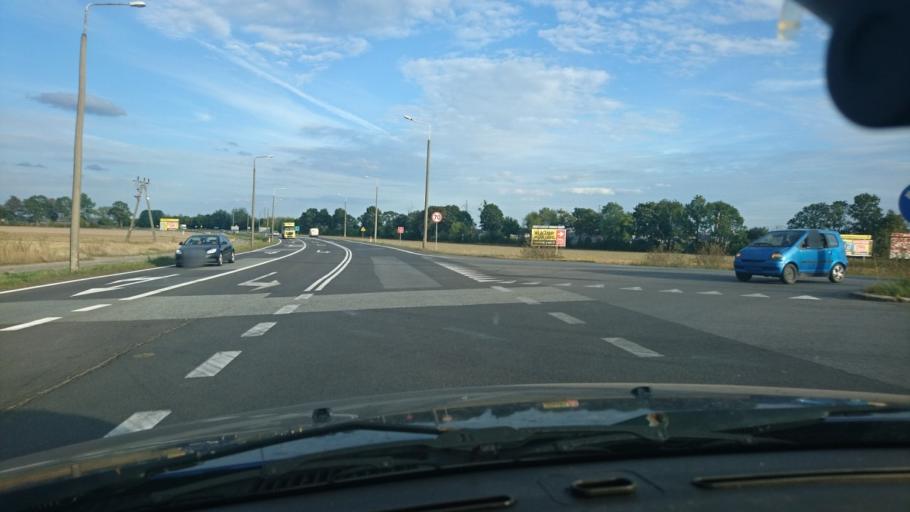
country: PL
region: Opole Voivodeship
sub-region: Powiat kluczborski
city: Kluczbork
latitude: 50.9930
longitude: 18.2110
